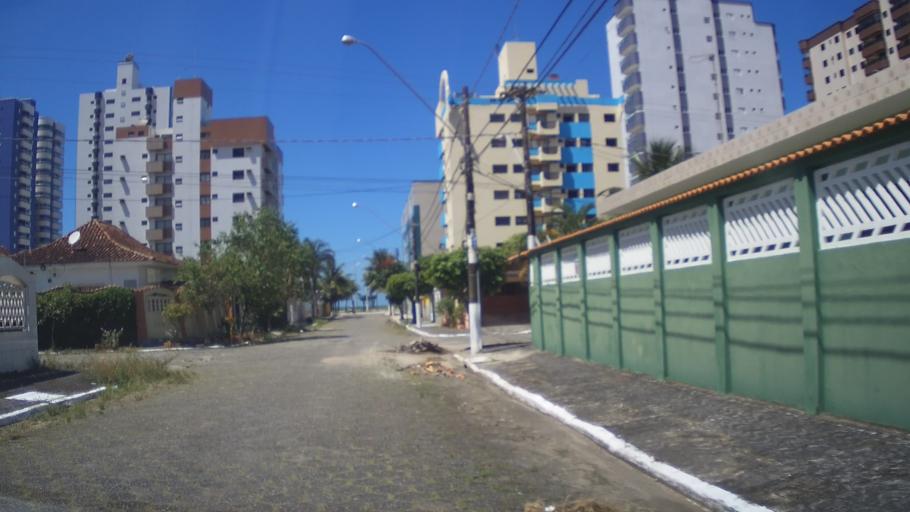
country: BR
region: Sao Paulo
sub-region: Mongagua
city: Mongagua
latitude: -24.0469
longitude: -46.5194
